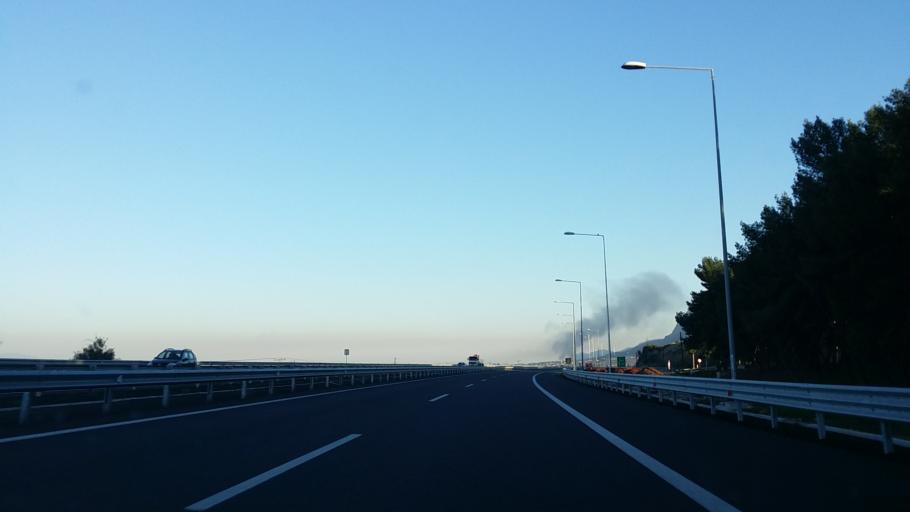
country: GR
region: Peloponnese
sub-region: Nomos Korinthias
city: Assos
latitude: 37.9209
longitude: 22.8162
